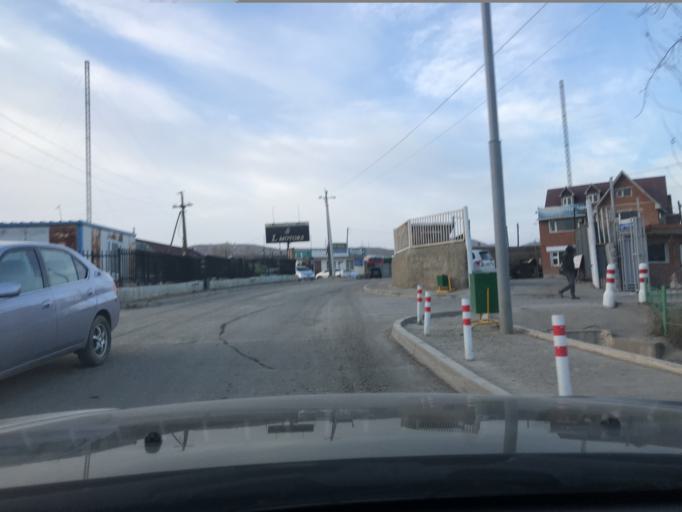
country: MN
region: Ulaanbaatar
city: Ulaanbaatar
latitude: 47.9293
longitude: 106.9974
